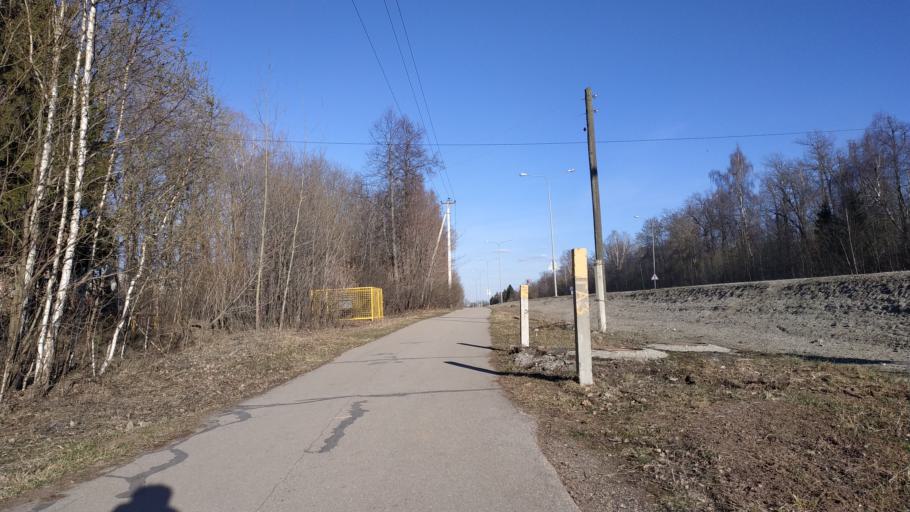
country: RU
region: Chuvashia
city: Novyye Lapsary
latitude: 56.1313
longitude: 47.1466
